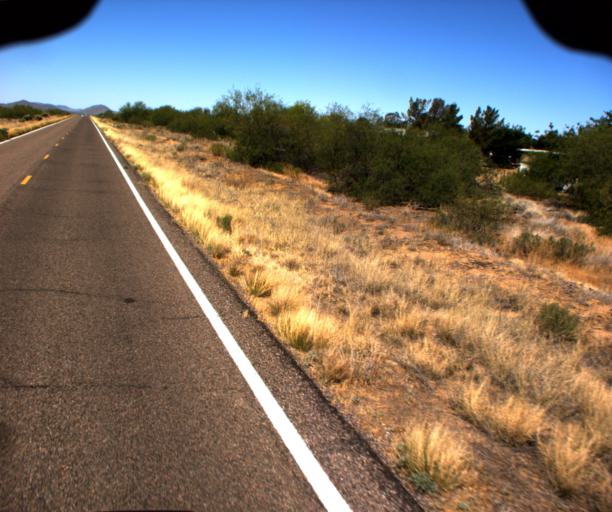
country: US
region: Arizona
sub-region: Yavapai County
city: Congress
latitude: 34.1542
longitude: -112.8730
